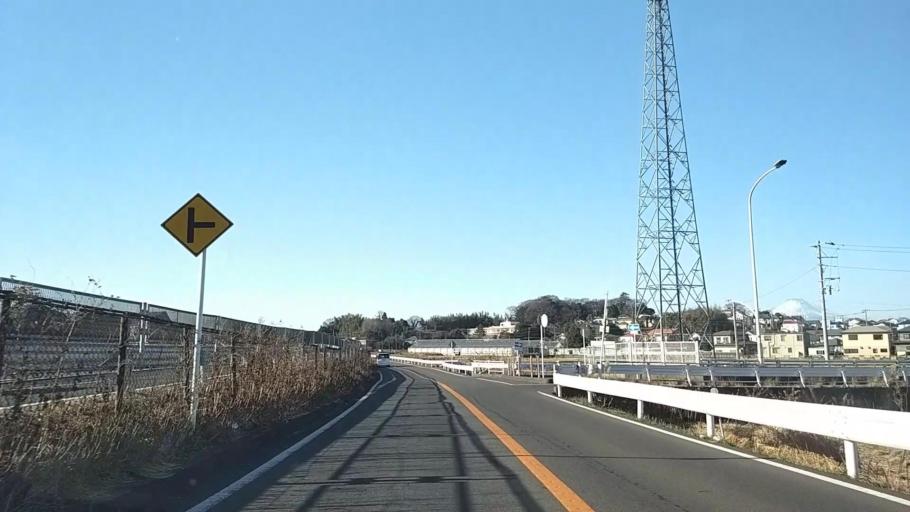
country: JP
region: Kanagawa
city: Isehara
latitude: 35.3727
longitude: 139.3150
